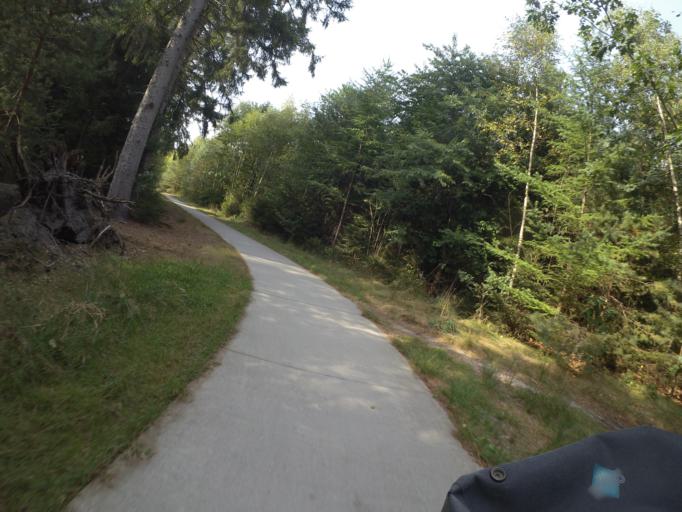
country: NL
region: Drenthe
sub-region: Gemeente Westerveld
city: Dwingeloo
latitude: 52.9037
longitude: 6.3637
